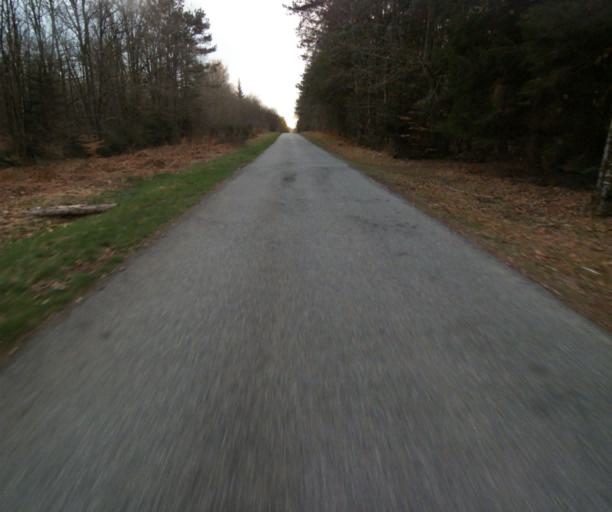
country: FR
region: Limousin
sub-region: Departement de la Correze
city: Correze
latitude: 45.2650
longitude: 1.9771
